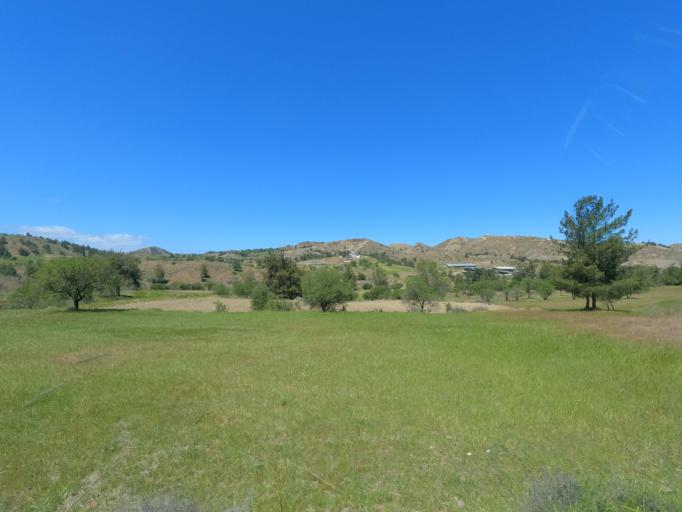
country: CY
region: Lefkosia
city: Peristerona
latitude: 35.0524
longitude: 33.0744
